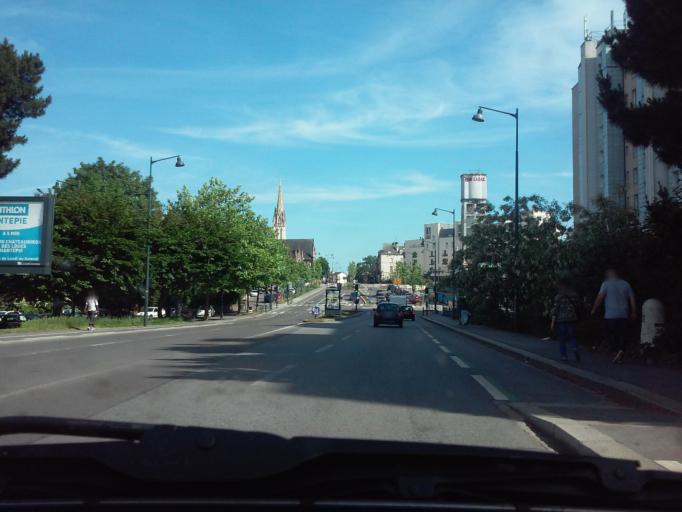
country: FR
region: Brittany
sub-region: Departement d'Ille-et-Vilaine
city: Rennes
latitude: 48.1042
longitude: -1.6637
